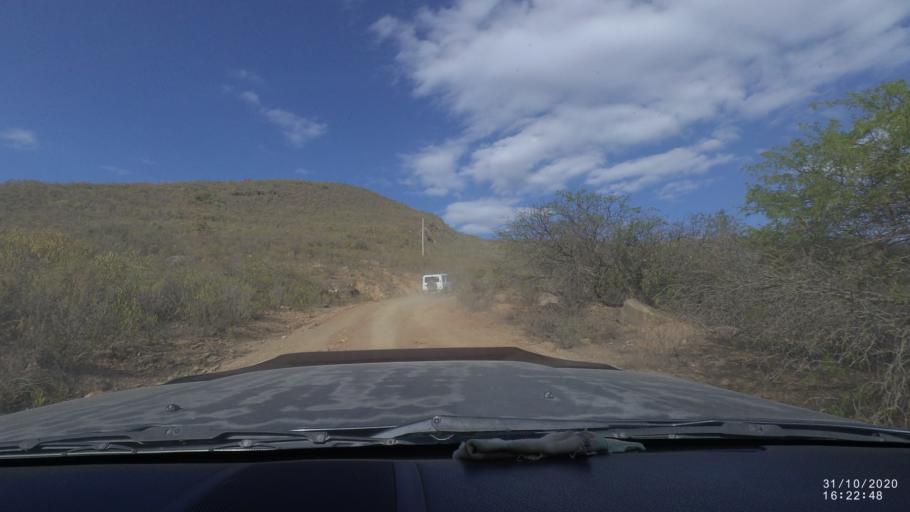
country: BO
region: Chuquisaca
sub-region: Provincia Zudanez
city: Mojocoya
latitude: -18.3996
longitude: -64.5921
